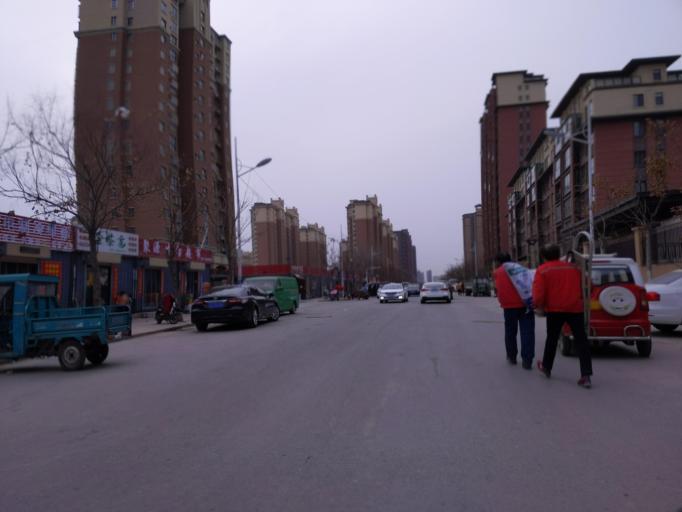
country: CN
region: Henan Sheng
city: Zhongyuanlu
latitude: 35.7422
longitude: 115.0768
